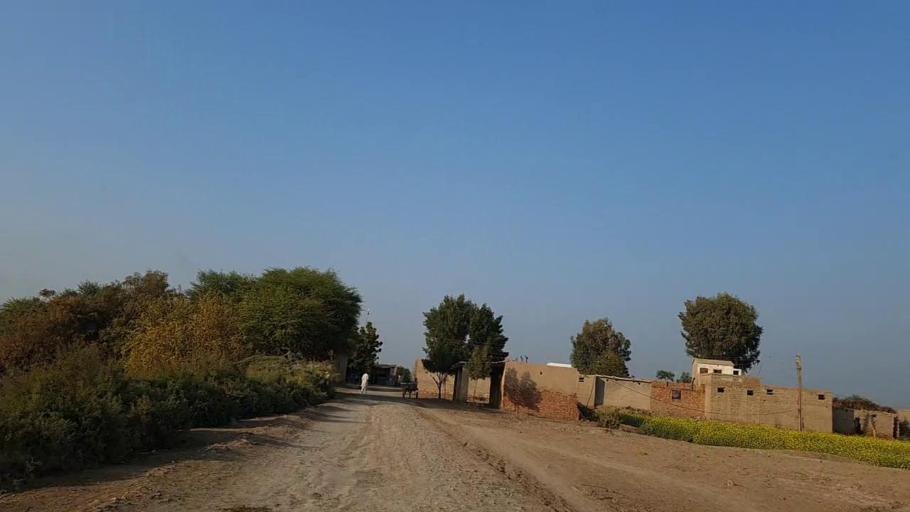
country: PK
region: Sindh
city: Sakrand
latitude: 26.1141
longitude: 68.3686
